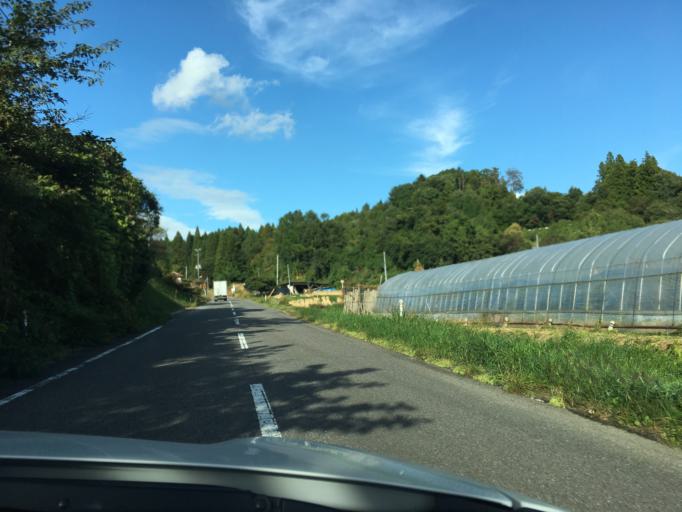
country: JP
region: Fukushima
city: Ishikawa
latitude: 37.2230
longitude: 140.4531
